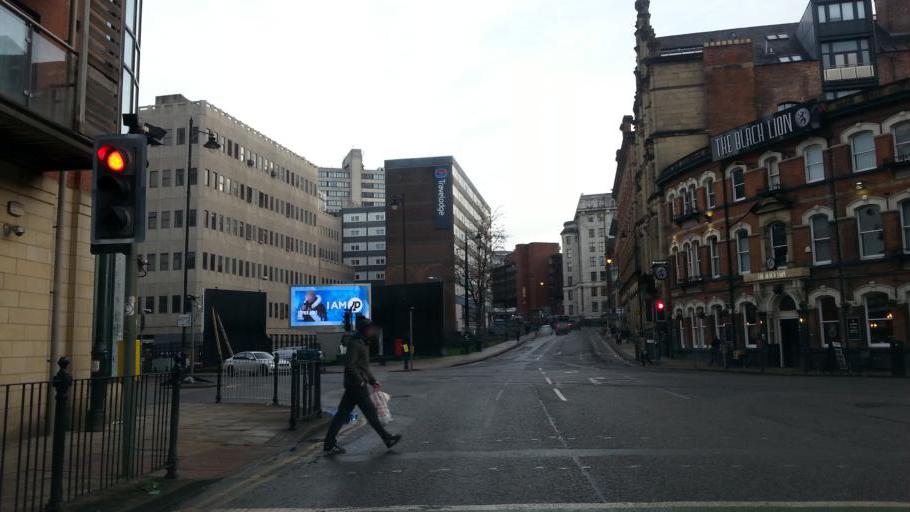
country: GB
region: England
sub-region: Manchester
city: Manchester
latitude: 53.4852
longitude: -2.2497
